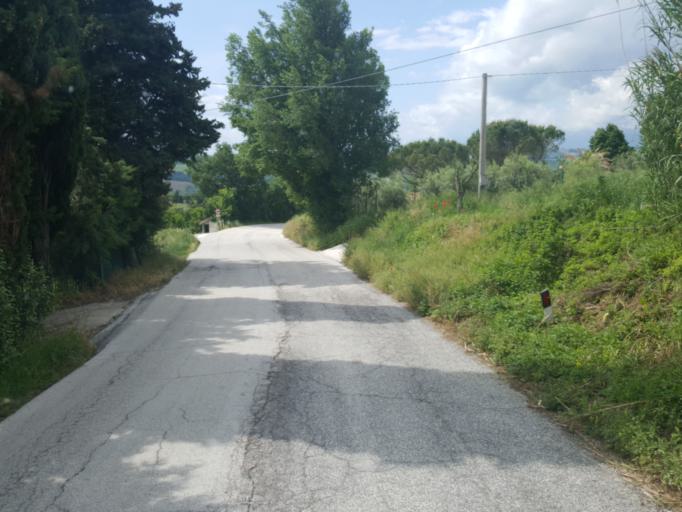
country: IT
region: The Marches
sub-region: Provincia di Macerata
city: Pollenza
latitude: 43.2553
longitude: 13.3687
